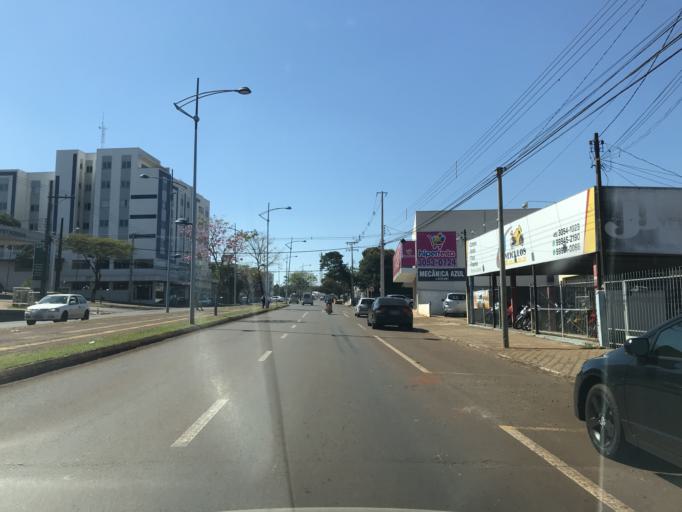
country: BR
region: Parana
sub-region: Toledo
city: Toledo
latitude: -24.7257
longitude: -53.7282
